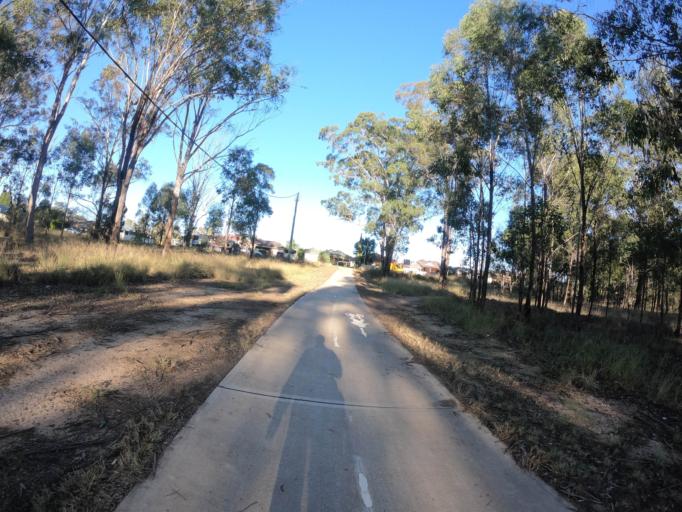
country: AU
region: New South Wales
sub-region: Hawkesbury
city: South Windsor
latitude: -33.6367
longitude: 150.8088
